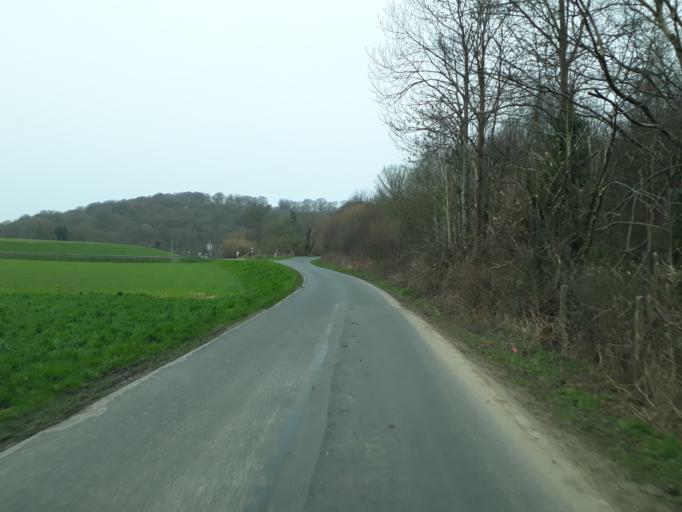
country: FR
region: Haute-Normandie
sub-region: Departement de la Seine-Maritime
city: Les Loges
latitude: 49.6769
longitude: 0.2572
